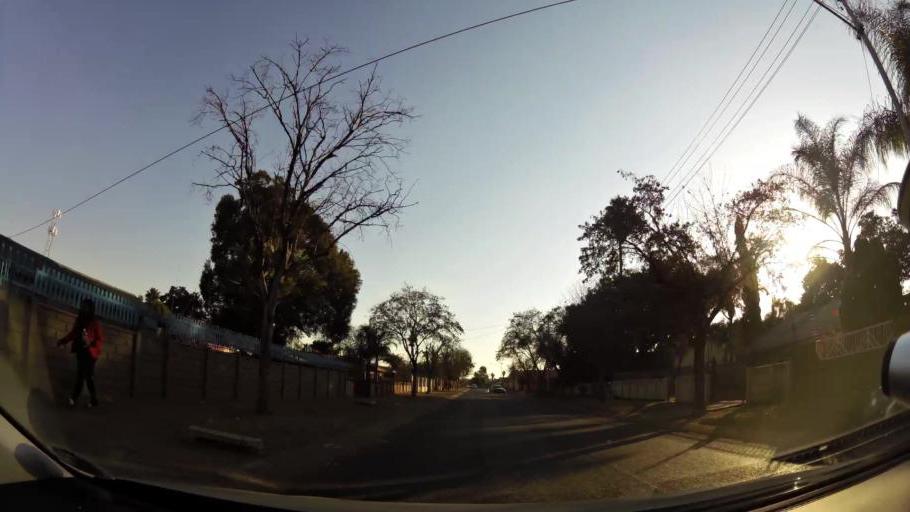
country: ZA
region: Gauteng
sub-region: City of Tshwane Metropolitan Municipality
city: Pretoria
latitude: -25.7420
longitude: 28.1230
